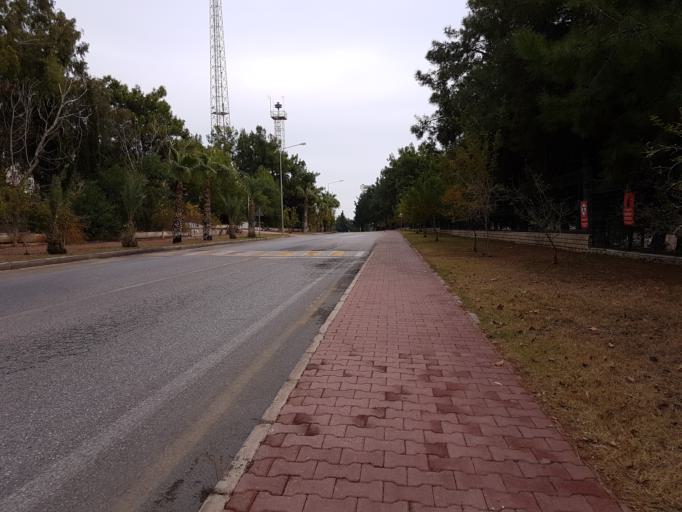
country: TR
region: Antalya
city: Antalya
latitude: 36.8538
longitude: 30.7913
